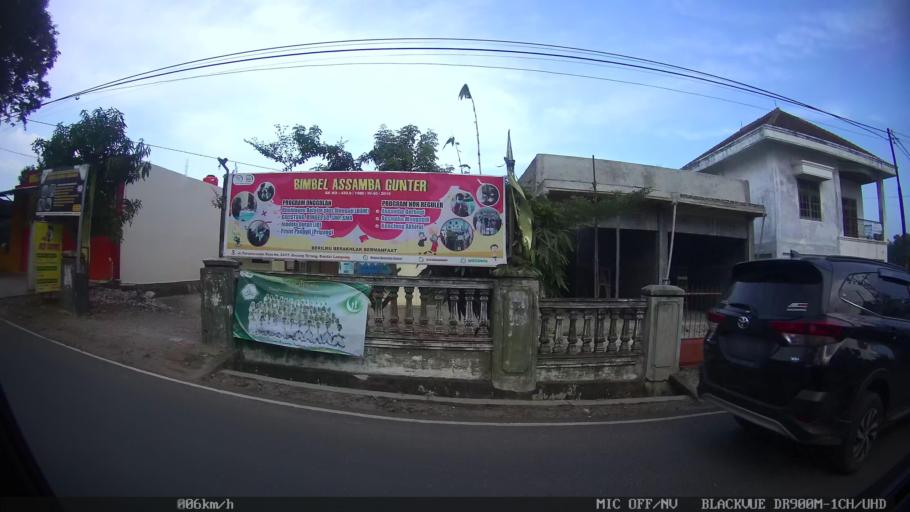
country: ID
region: Lampung
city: Kedaton
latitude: -5.3894
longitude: 105.2327
